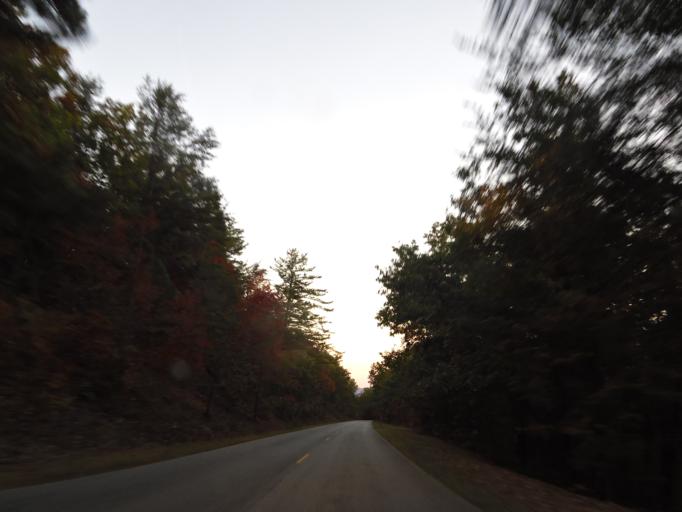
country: US
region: Tennessee
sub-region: Blount County
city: Maryville
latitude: 35.6611
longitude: -83.9137
